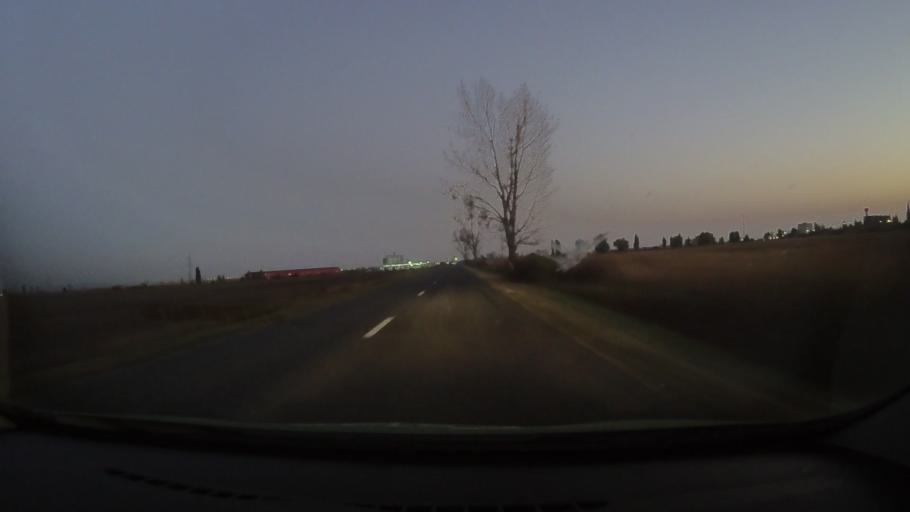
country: RO
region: Arad
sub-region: Comuna Vladimirescu
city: Vladimirescu
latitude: 46.1923
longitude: 21.3913
